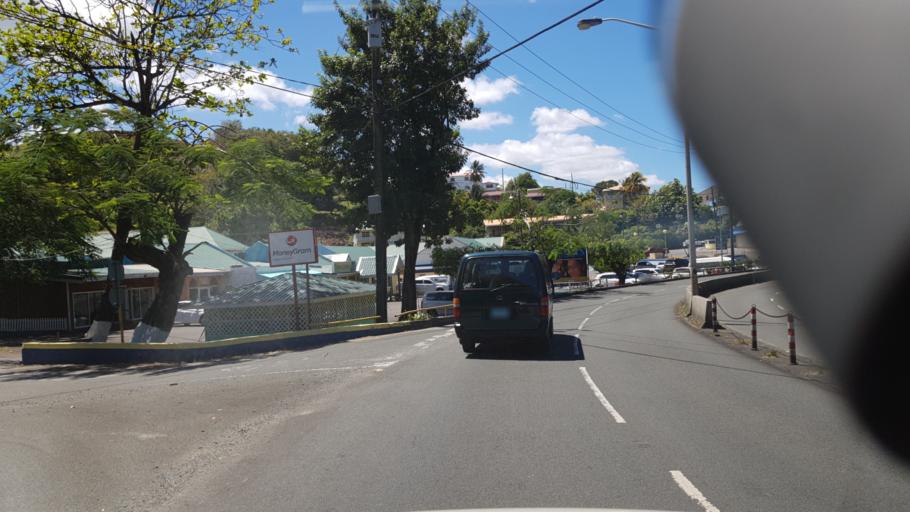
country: LC
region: Castries Quarter
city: Bisee
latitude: 14.0302
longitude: -60.9757
